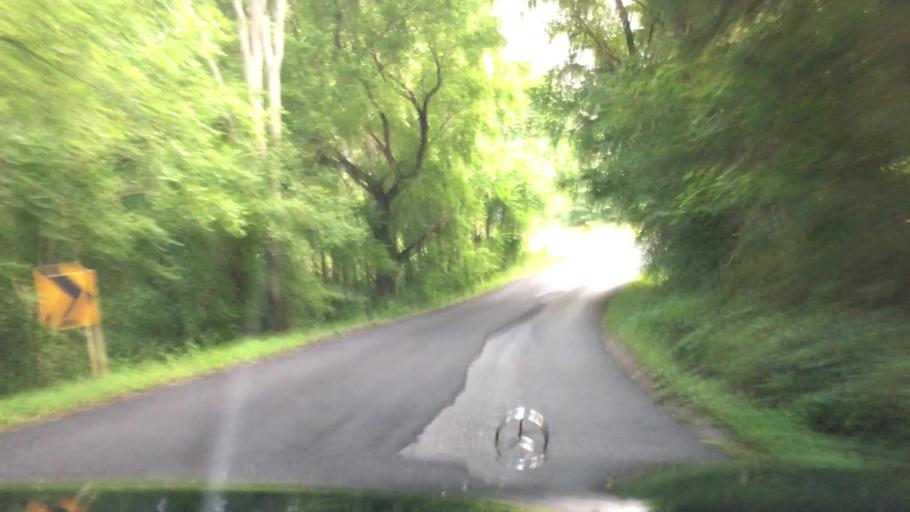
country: US
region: Virginia
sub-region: Campbell County
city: Timberlake
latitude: 37.2582
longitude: -79.3149
